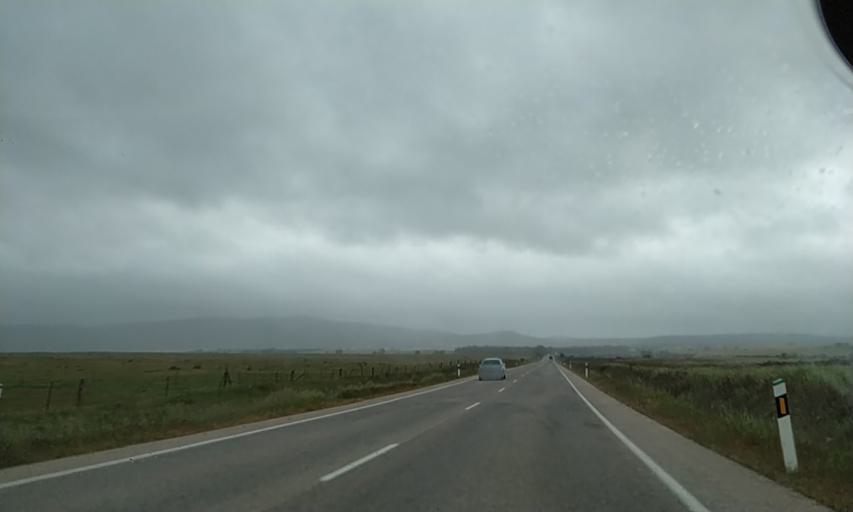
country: ES
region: Extremadura
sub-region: Provincia de Caceres
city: Malpartida de Caceres
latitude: 39.3410
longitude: -6.4776
